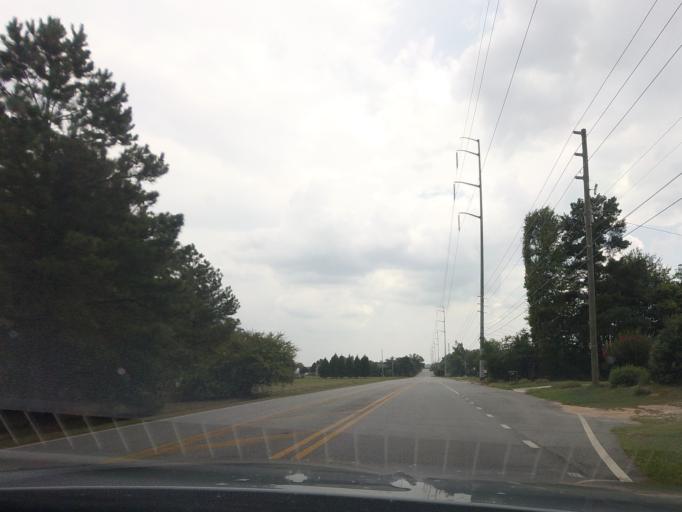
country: US
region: Georgia
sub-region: Bibb County
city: West Point
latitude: 32.8176
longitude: -83.7455
